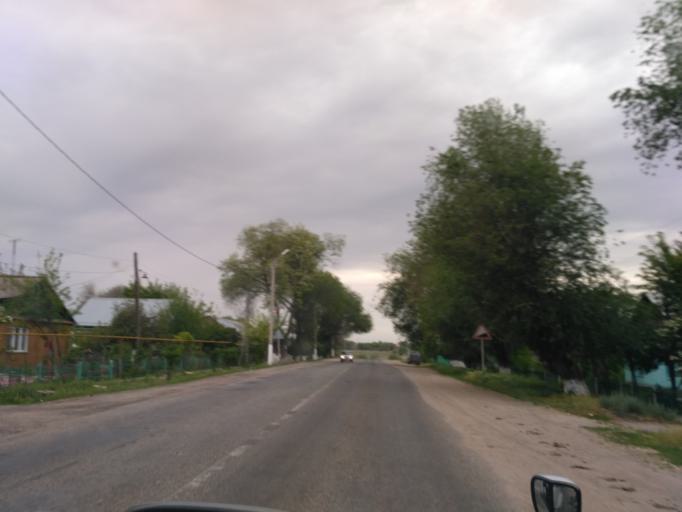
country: KZ
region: Almaty Oblysy
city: Burunday
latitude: 43.4609
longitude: 76.7231
